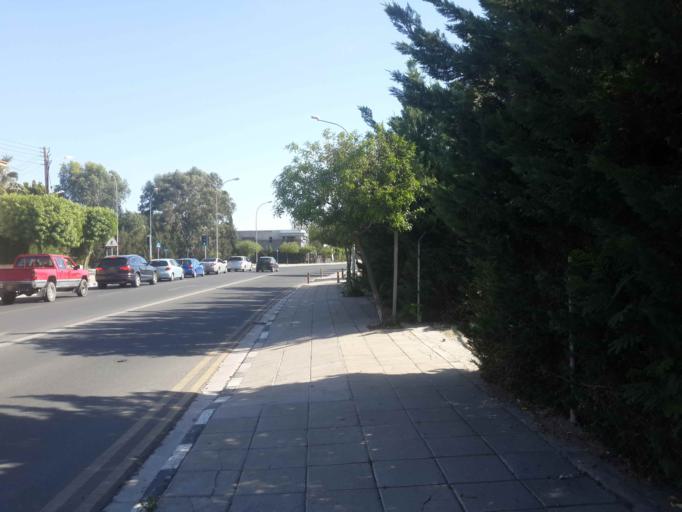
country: CY
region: Lefkosia
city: Nicosia
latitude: 35.1476
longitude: 33.3339
